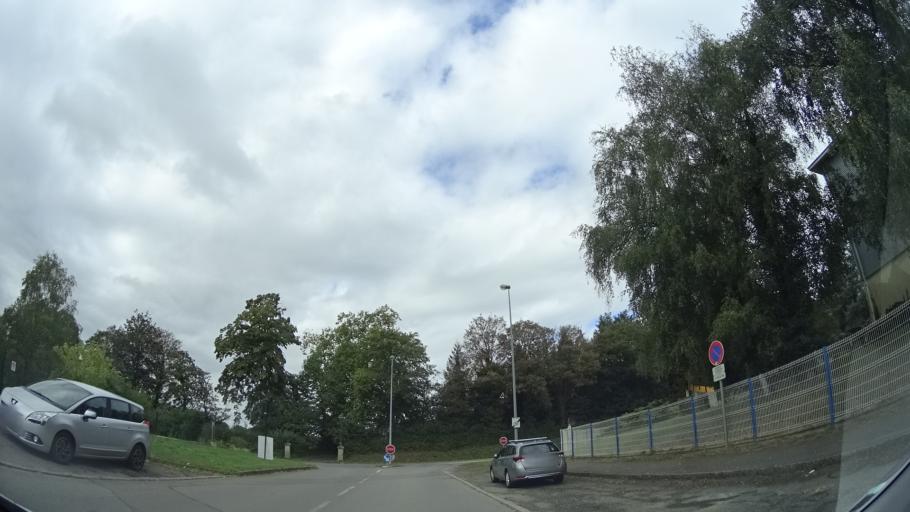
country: FR
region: Brittany
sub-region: Departement d'Ille-et-Vilaine
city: Chasne-sur-Illet
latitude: 48.2591
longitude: -1.6051
